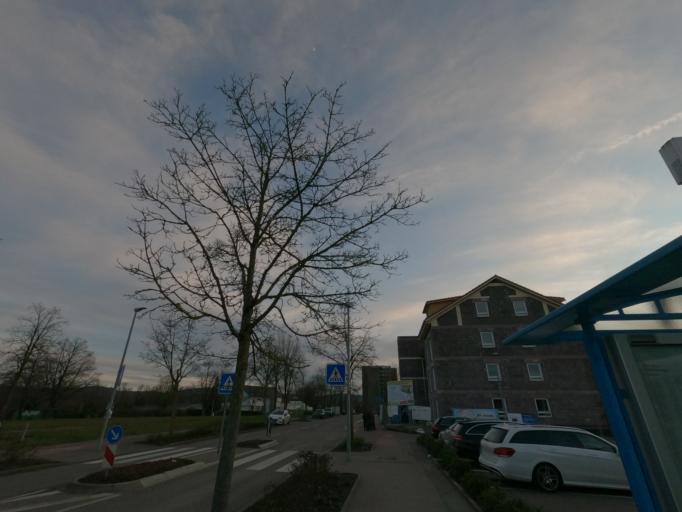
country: DE
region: Baden-Wuerttemberg
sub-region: Regierungsbezirk Stuttgart
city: Goeppingen
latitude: 48.7099
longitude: 9.6751
